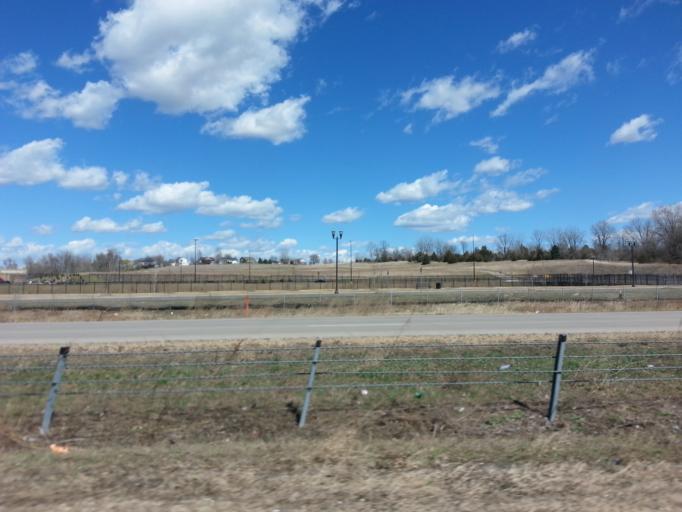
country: US
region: Minnesota
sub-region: Washington County
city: Cottage Grove
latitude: 44.8078
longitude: -92.9185
